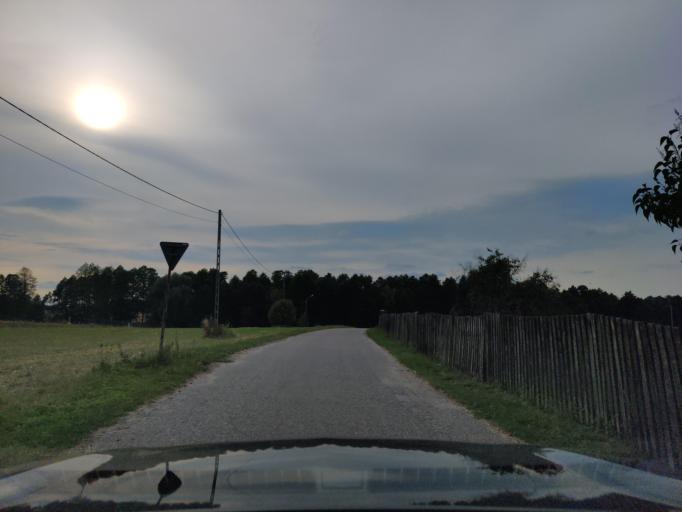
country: PL
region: Masovian Voivodeship
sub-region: Powiat pultuski
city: Obryte
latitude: 52.7411
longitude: 21.2520
